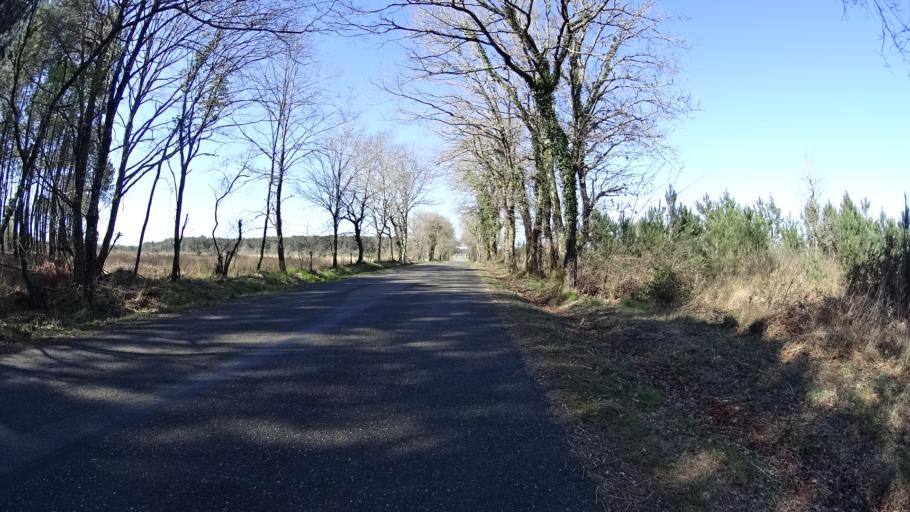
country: FR
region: Aquitaine
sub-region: Departement des Landes
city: Mees
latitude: 43.7342
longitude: -1.0947
